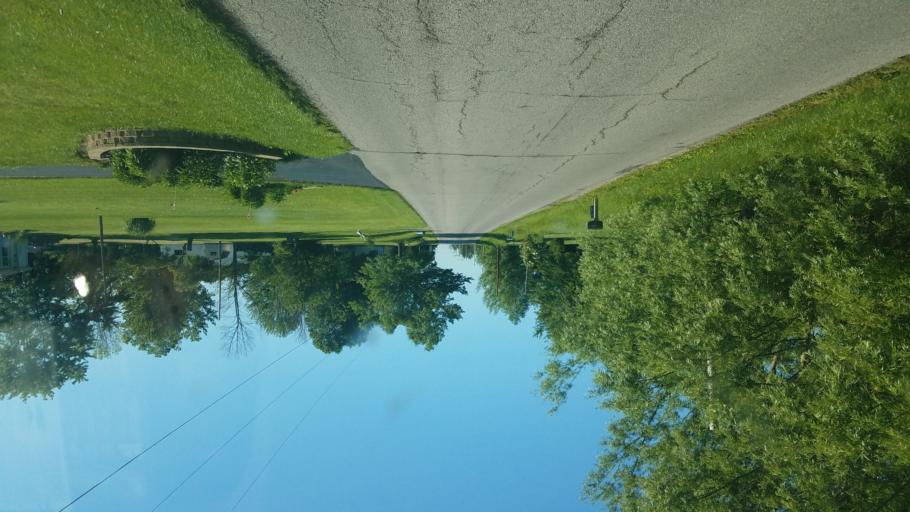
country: US
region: Ohio
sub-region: Crawford County
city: Bucyrus
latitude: 40.7820
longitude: -82.9587
